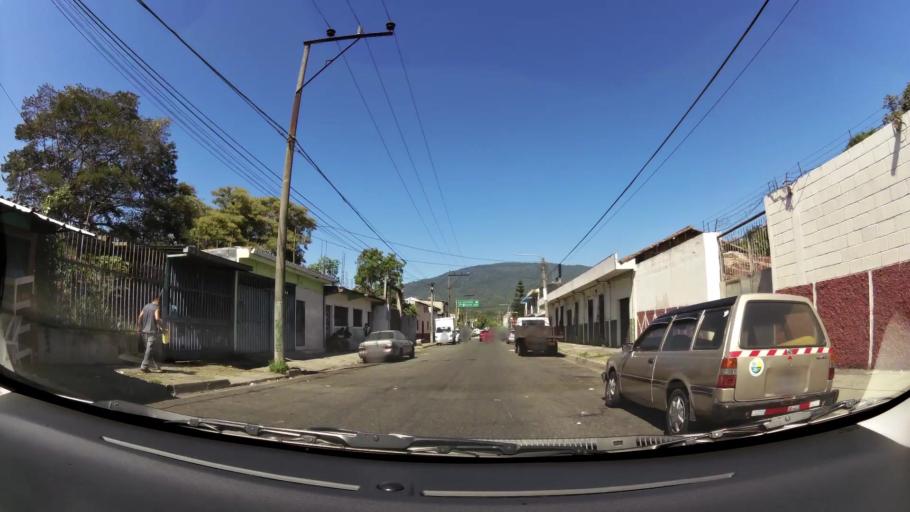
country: SV
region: La Libertad
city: Santa Tecla
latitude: 13.6727
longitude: -89.2949
